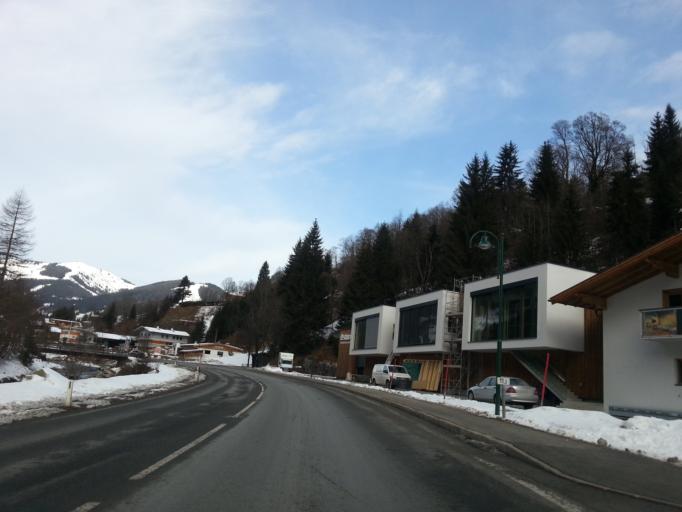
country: AT
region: Salzburg
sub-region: Politischer Bezirk Zell am See
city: Saalbach
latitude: 47.3829
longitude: 12.6667
